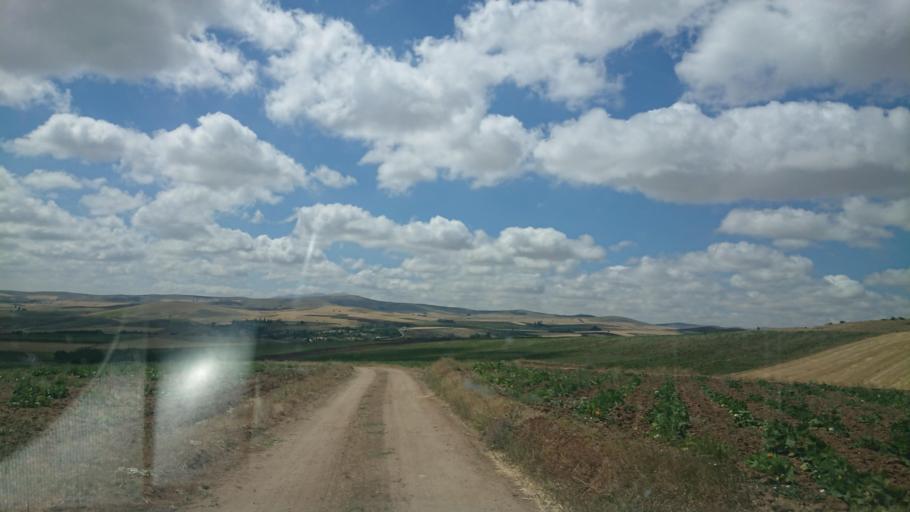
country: TR
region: Aksaray
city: Agacoren
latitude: 38.8341
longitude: 33.9481
